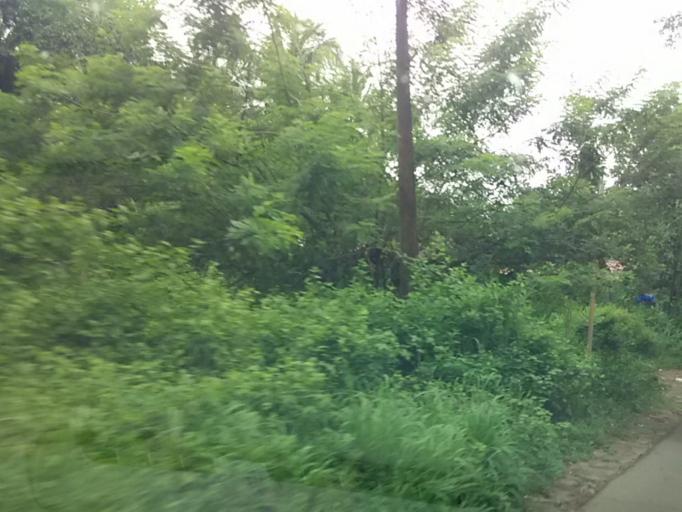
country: IN
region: Kerala
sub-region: Kozhikode
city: Kunnamangalam
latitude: 11.3067
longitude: 75.8986
